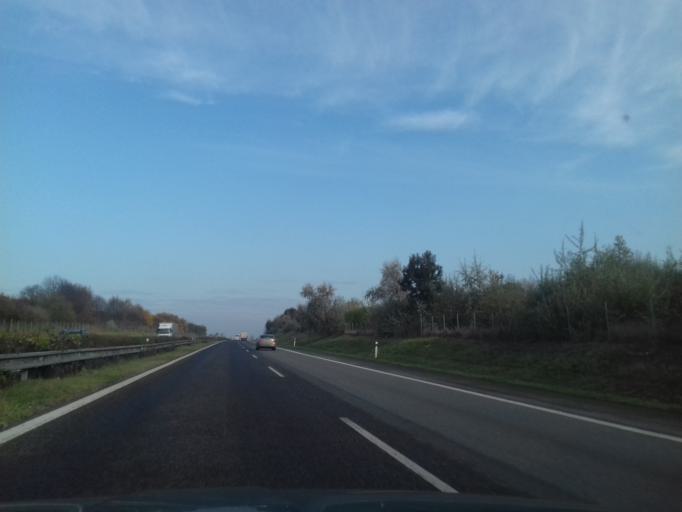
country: SK
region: Bratislavsky
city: Stupava
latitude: 48.2710
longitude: 17.0089
